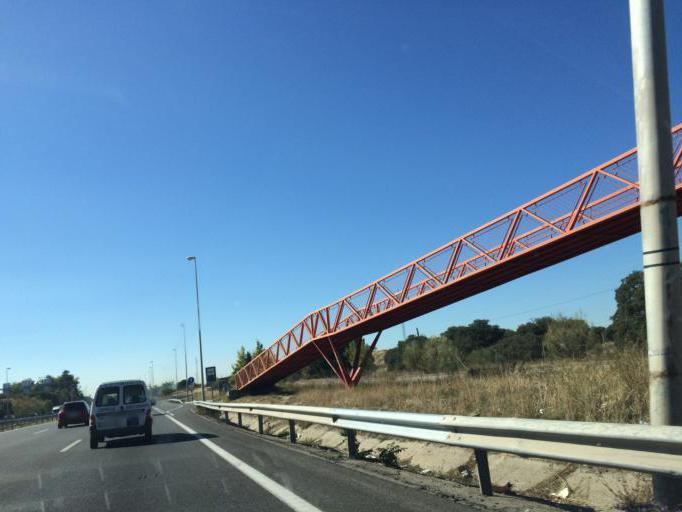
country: ES
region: Madrid
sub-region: Provincia de Madrid
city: Tres Cantos
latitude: 40.5782
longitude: -3.7063
